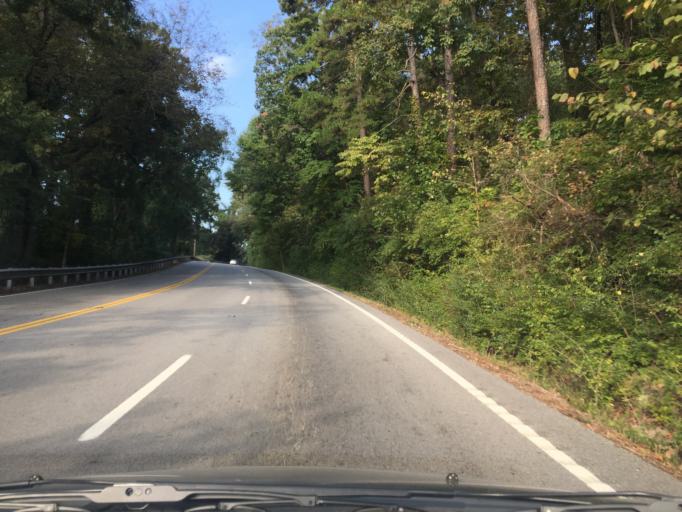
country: US
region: Tennessee
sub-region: Hamilton County
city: Signal Mountain
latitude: 35.1047
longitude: -85.3450
